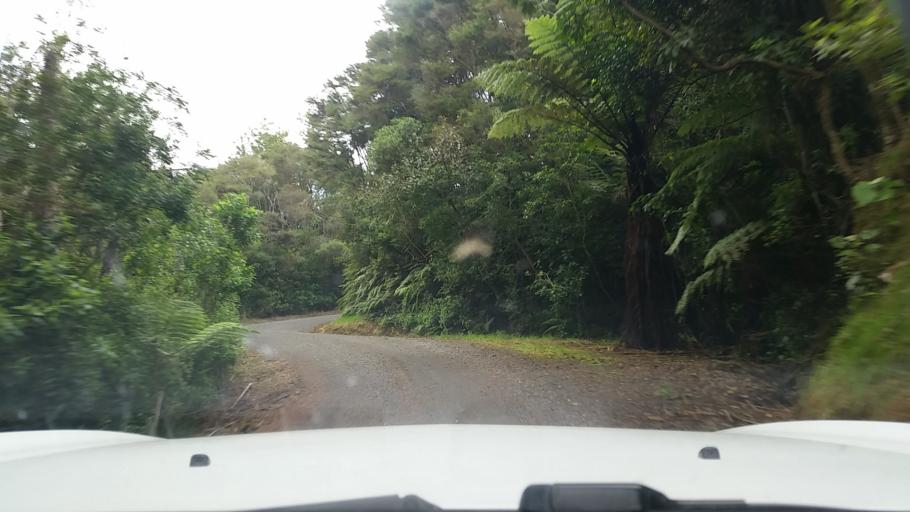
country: NZ
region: Waikato
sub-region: Hauraki District
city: Ngatea
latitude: -37.4616
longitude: 175.4704
